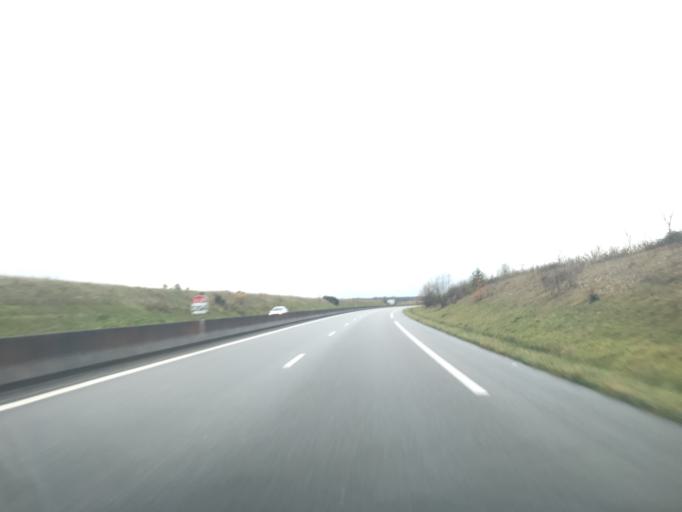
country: FR
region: Haute-Normandie
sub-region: Departement de l'Eure
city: Brionne
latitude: 49.1884
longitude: 0.7665
